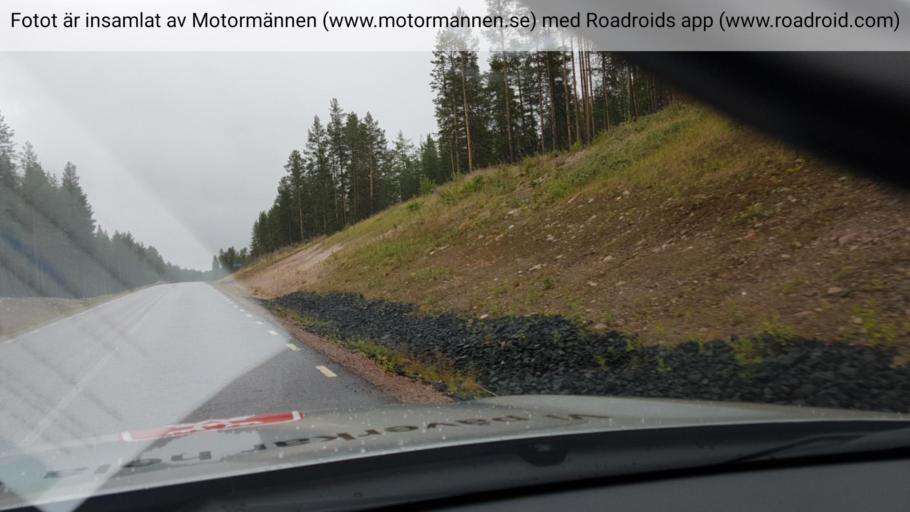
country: SE
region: Norrbotten
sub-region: Gallivare Kommun
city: Gaellivare
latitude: 66.6761
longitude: 20.3669
